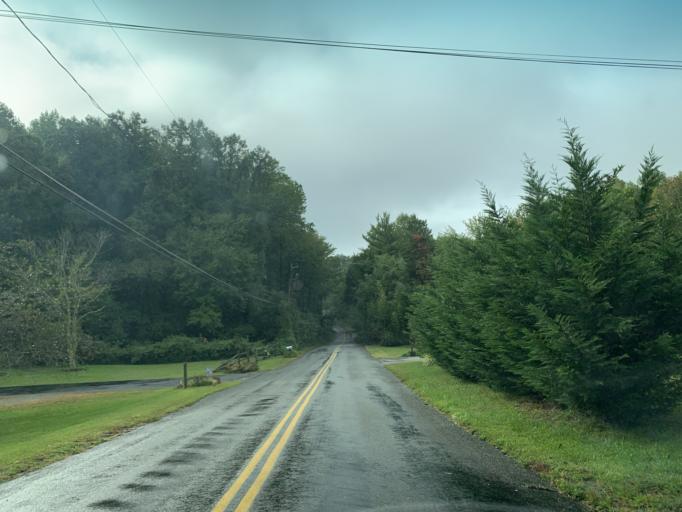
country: US
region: Maryland
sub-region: Harford County
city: Aberdeen
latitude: 39.5656
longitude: -76.1581
